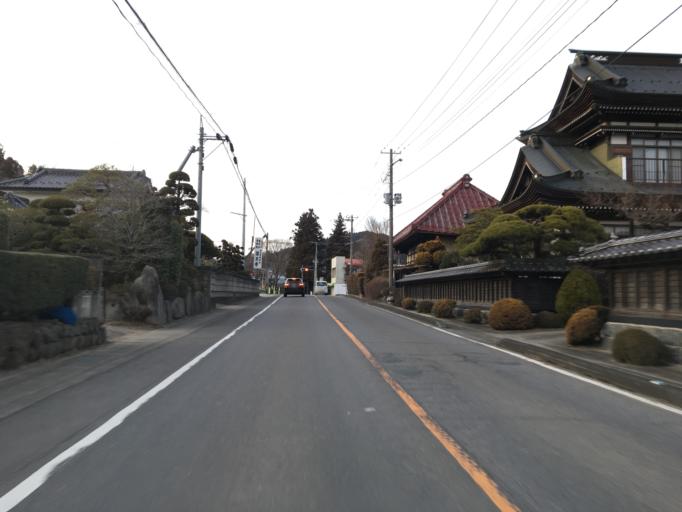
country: JP
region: Ibaraki
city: Daigo
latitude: 36.9521
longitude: 140.4069
